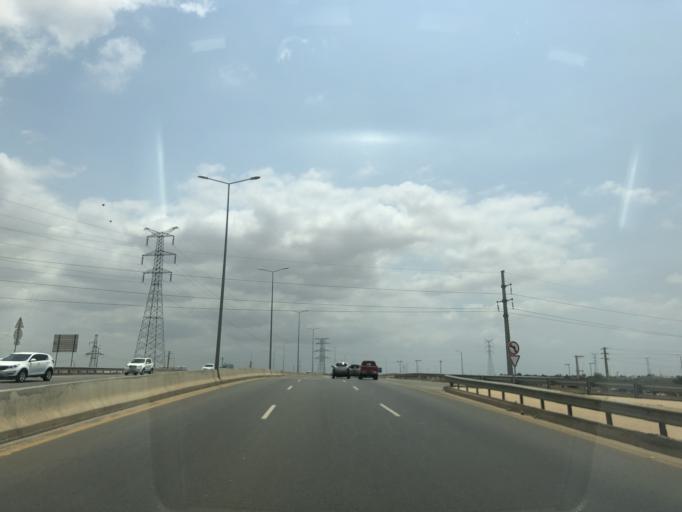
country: AO
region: Luanda
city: Luanda
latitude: -8.9722
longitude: 13.2543
